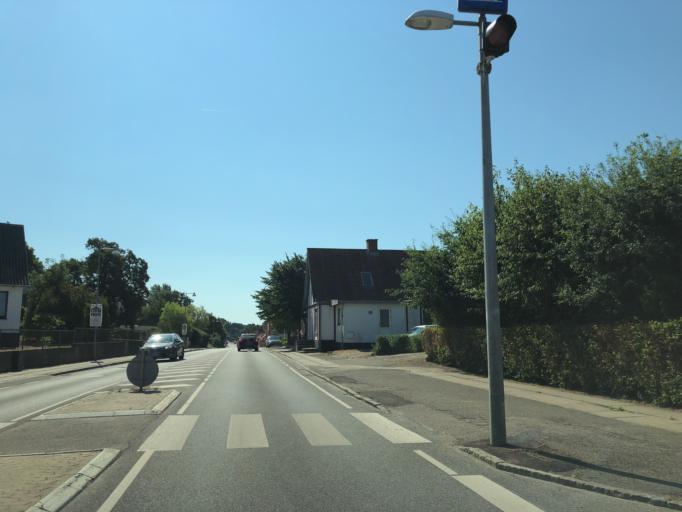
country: DK
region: Zealand
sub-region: Odsherred Kommune
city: Asnaes
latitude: 55.9683
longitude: 11.3641
